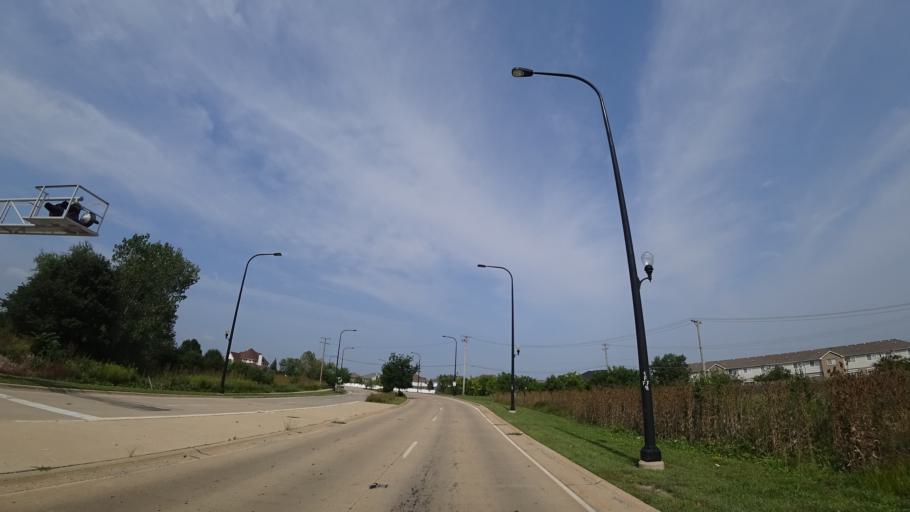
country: US
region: Illinois
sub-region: Cook County
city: Orland Hills
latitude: 41.5576
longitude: -87.8254
